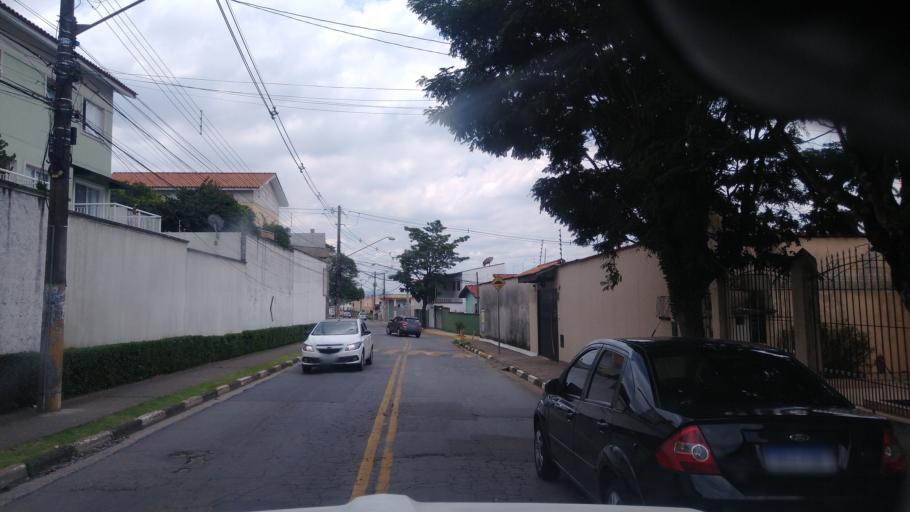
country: BR
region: Sao Paulo
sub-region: Suzano
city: Suzano
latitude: -23.5588
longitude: -46.3218
